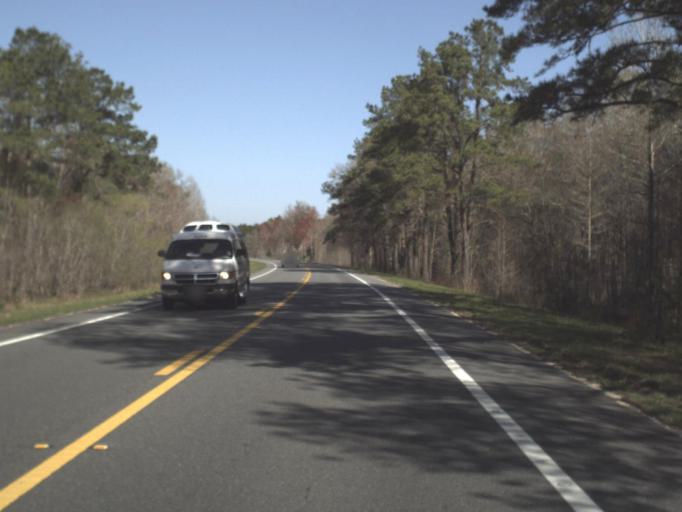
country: US
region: Florida
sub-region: Leon County
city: Woodville
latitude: 30.1783
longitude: -84.0108
